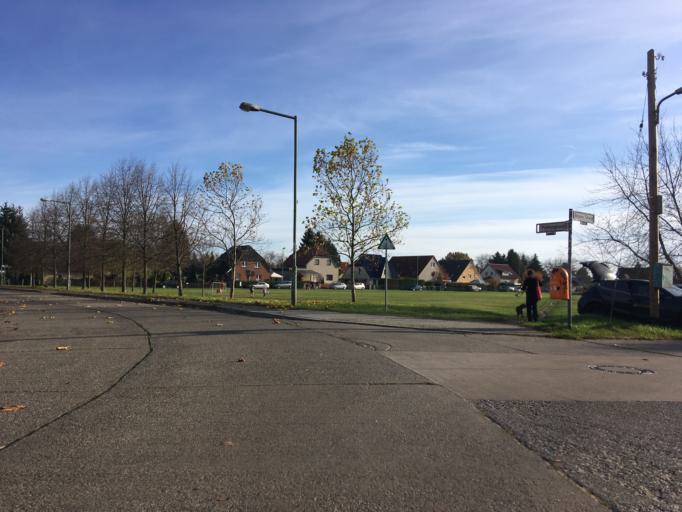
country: DE
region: Berlin
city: Biesdorf
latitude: 52.4982
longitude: 13.5486
